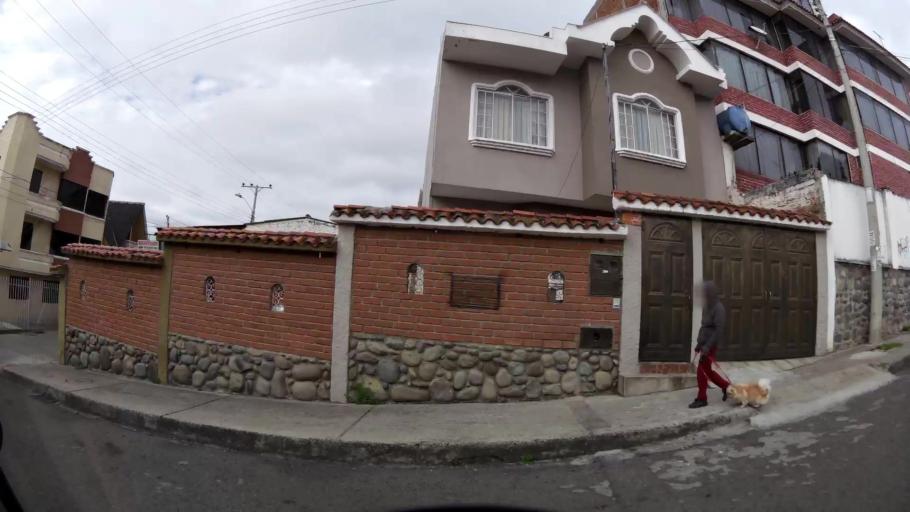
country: EC
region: Azuay
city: Cuenca
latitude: -2.8937
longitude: -78.9816
